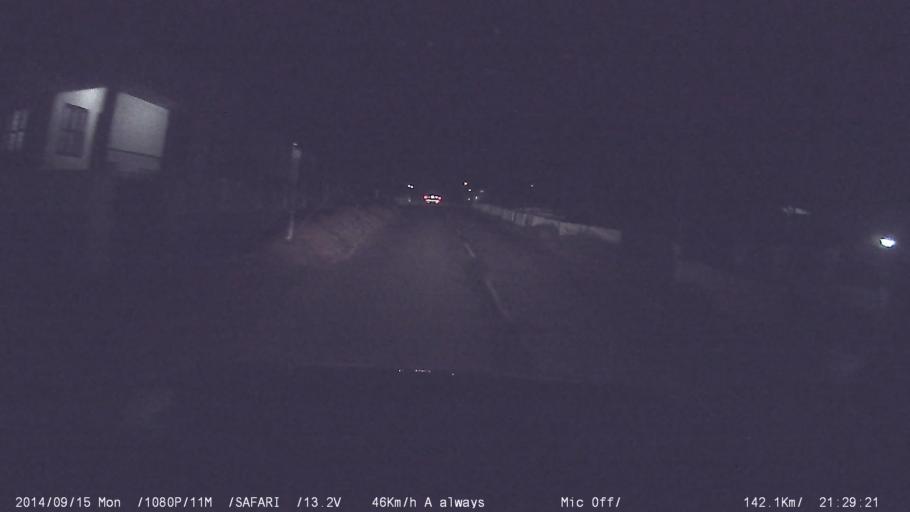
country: IN
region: Kerala
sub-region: Kottayam
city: Palackattumala
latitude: 9.6869
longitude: 76.5573
